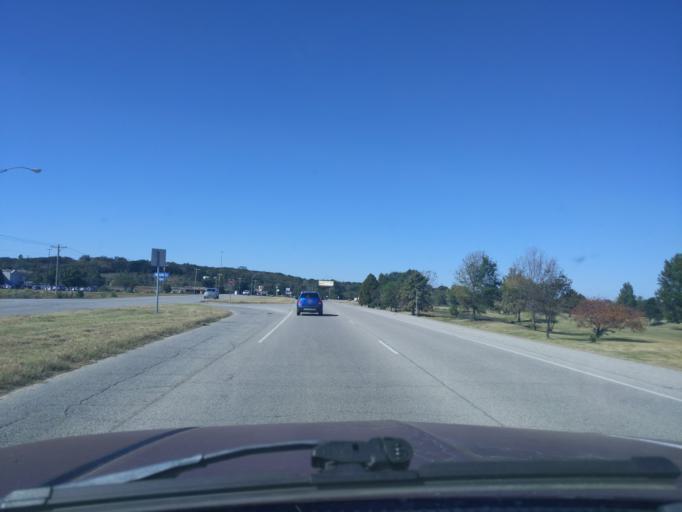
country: US
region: Oklahoma
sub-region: Creek County
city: Sapulpa
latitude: 35.9884
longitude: -96.1316
